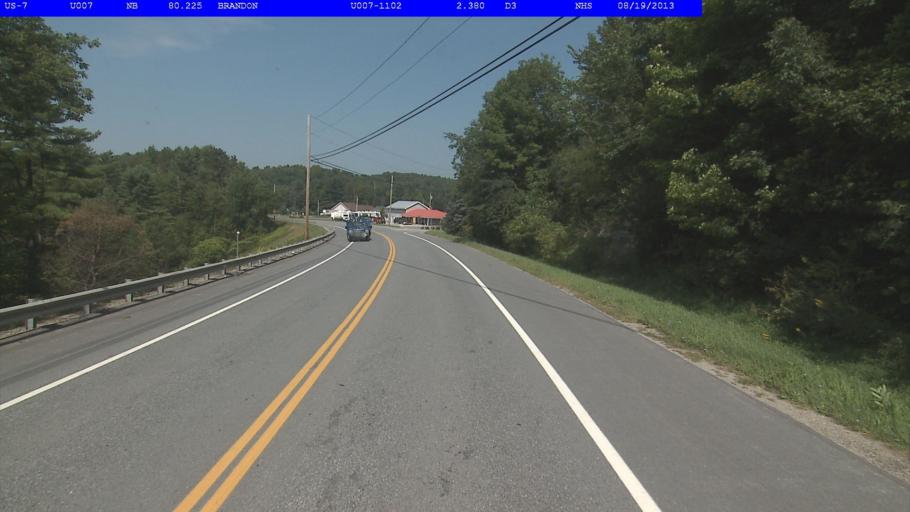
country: US
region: Vermont
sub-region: Rutland County
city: Brandon
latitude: 43.7851
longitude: -73.0651
